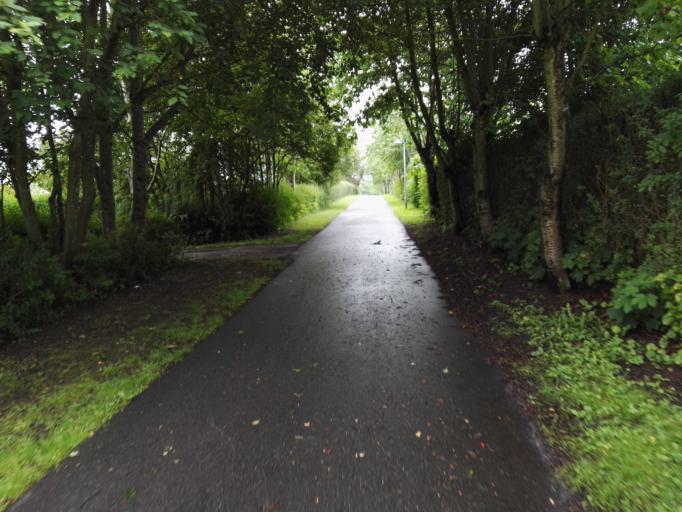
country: DK
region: Capital Region
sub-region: Egedal Kommune
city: Olstykke
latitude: 55.7716
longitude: 12.1629
